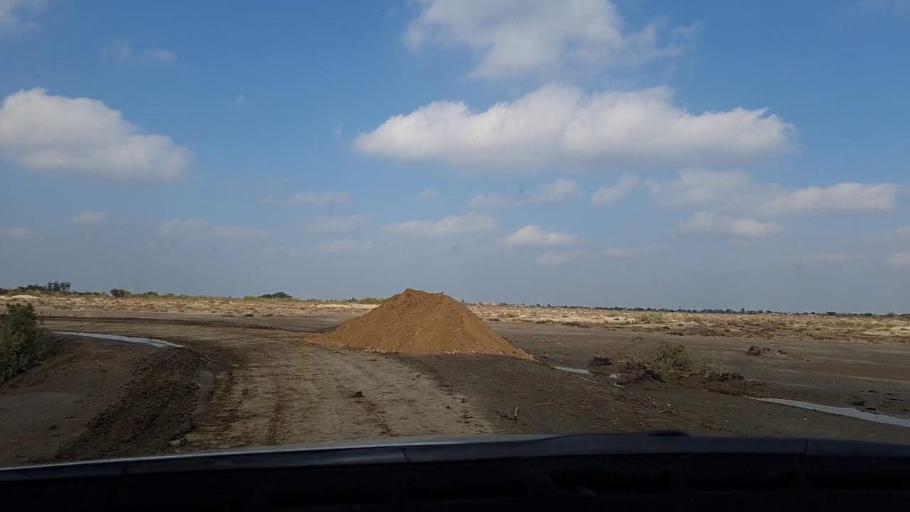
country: PK
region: Sindh
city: Tando Mittha Khan
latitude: 25.7662
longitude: 69.2687
